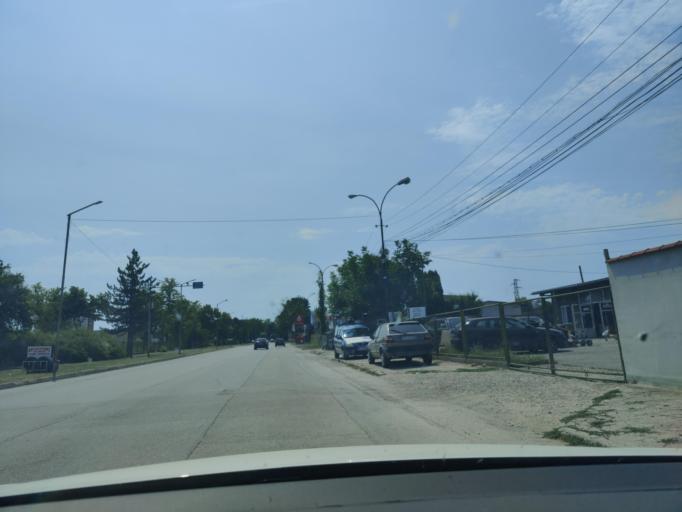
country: BG
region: Montana
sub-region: Obshtina Montana
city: Montana
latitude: 43.4300
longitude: 23.2307
